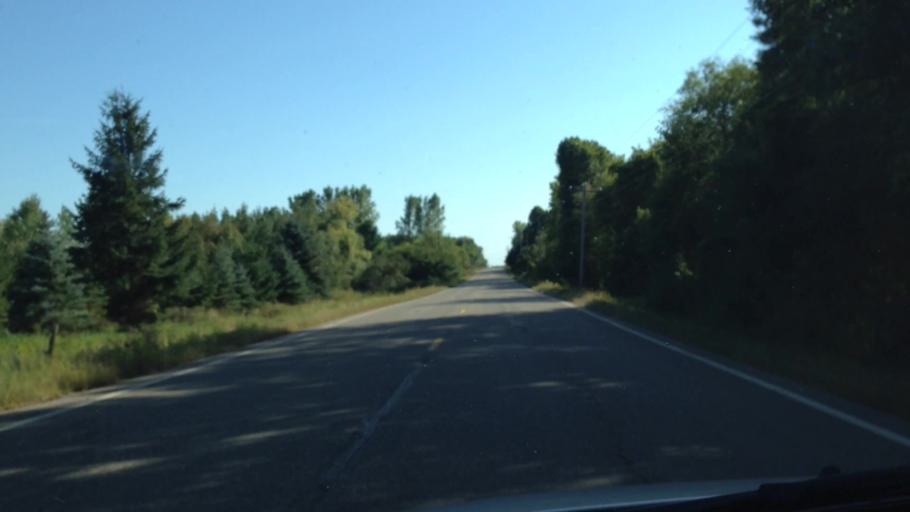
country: US
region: Minnesota
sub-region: Washington County
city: Stillwater
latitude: 45.0926
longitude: -92.8129
